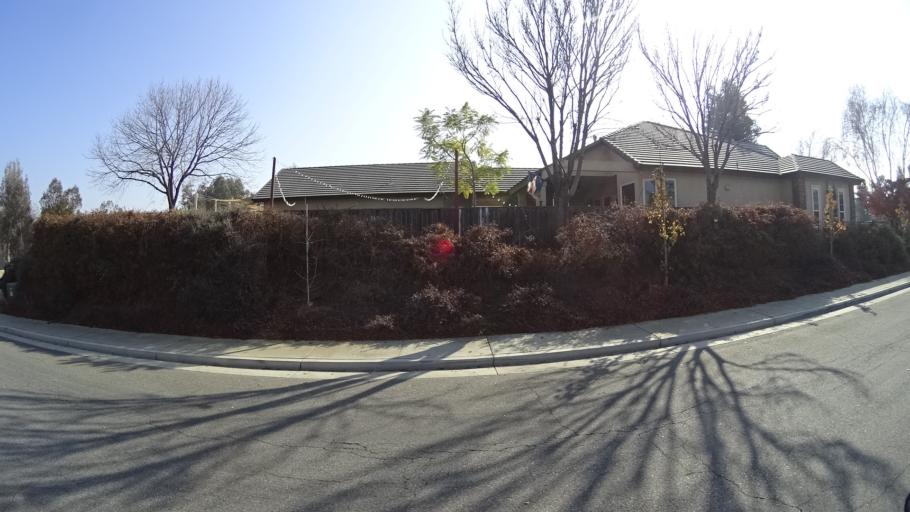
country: US
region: California
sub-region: Kern County
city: Oildale
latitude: 35.4066
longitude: -118.8682
